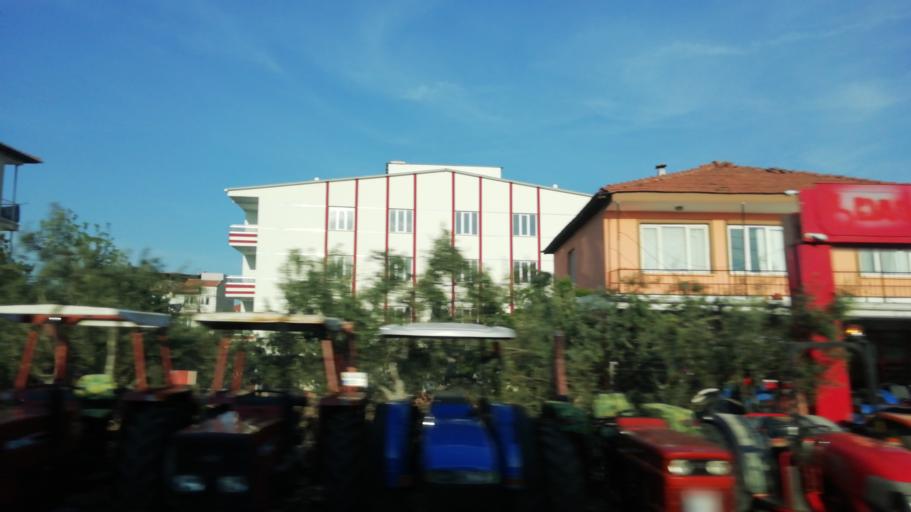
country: TR
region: Manisa
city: Akhisar
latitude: 38.9328
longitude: 27.8348
